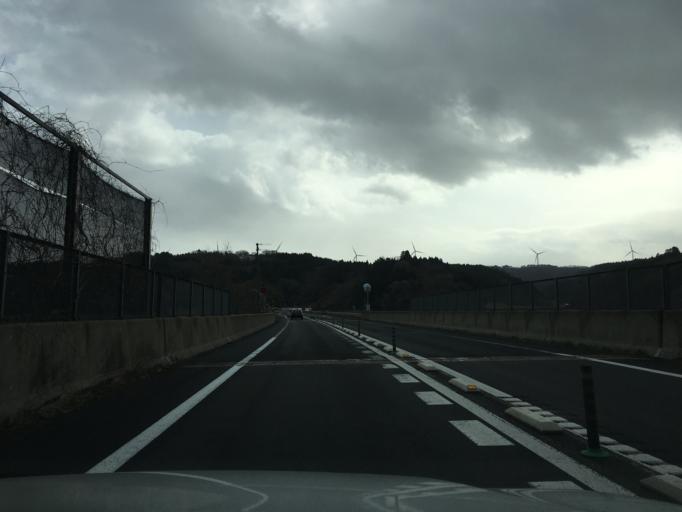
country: JP
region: Yamagata
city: Yuza
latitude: 39.3185
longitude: 140.0063
